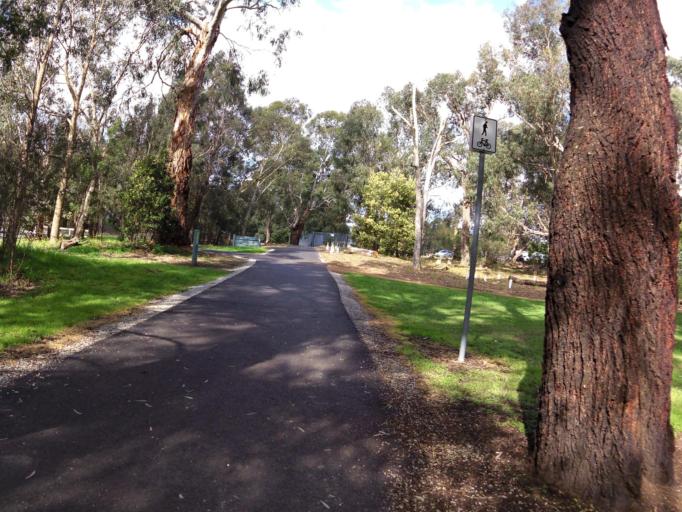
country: AU
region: Victoria
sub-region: Knox
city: Bayswater
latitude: -37.8374
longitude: 145.2673
